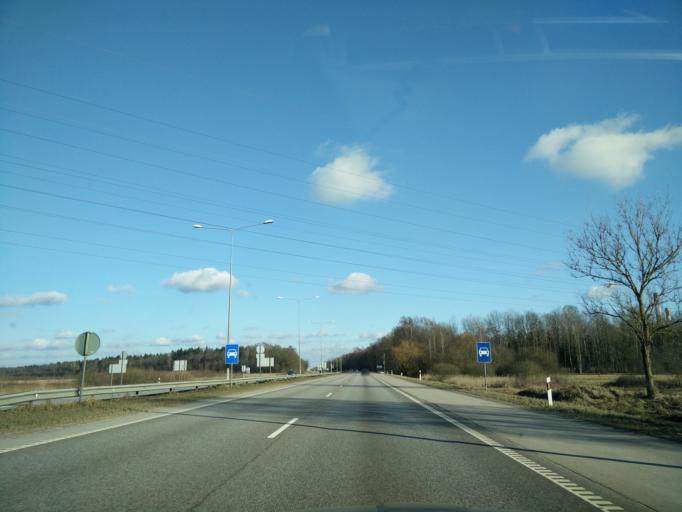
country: LT
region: Kauno apskritis
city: Dainava (Kaunas)
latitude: 54.9311
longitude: 23.9986
